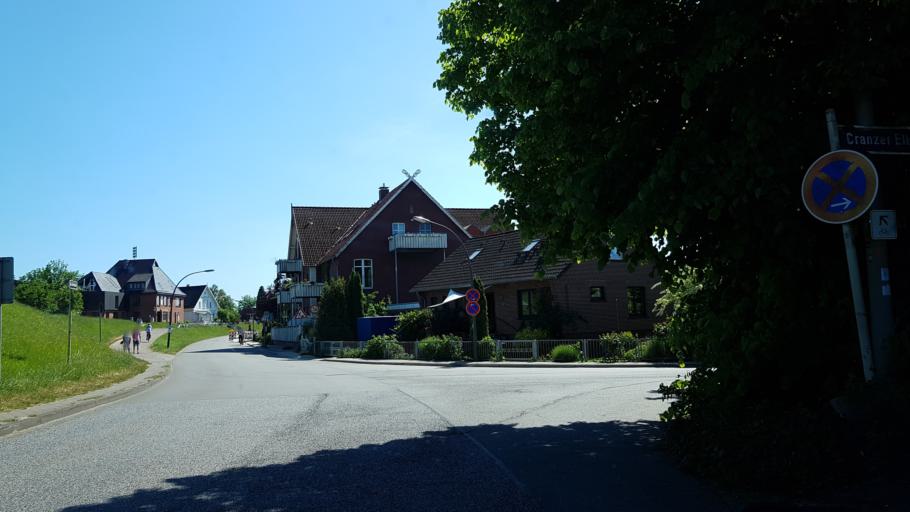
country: DE
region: Lower Saxony
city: Neu Wulmstorf
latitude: 53.5371
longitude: 9.7807
